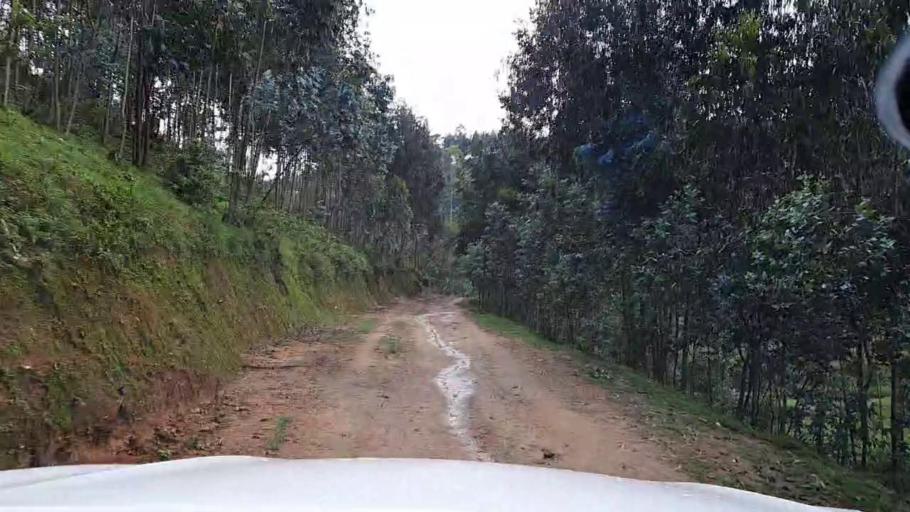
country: BI
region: Kayanza
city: Kayanza
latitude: -2.7778
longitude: 29.4480
